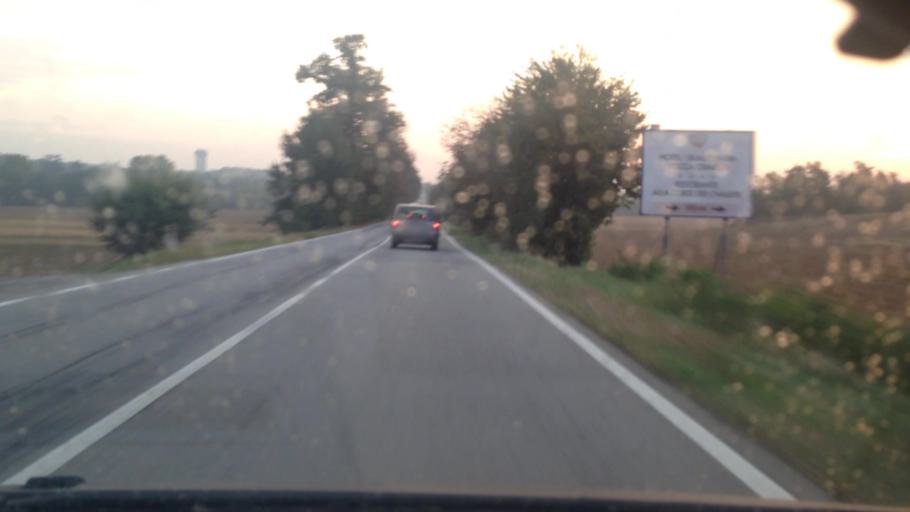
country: IT
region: Piedmont
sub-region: Provincia di Asti
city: Cerro Tanaro
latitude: 44.8905
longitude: 8.3779
